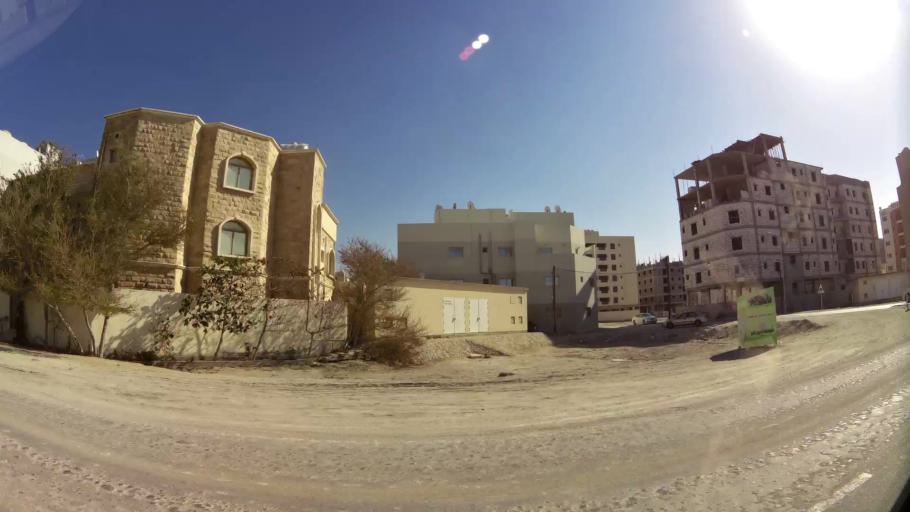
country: BH
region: Muharraq
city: Al Hadd
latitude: 26.2340
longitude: 50.6483
